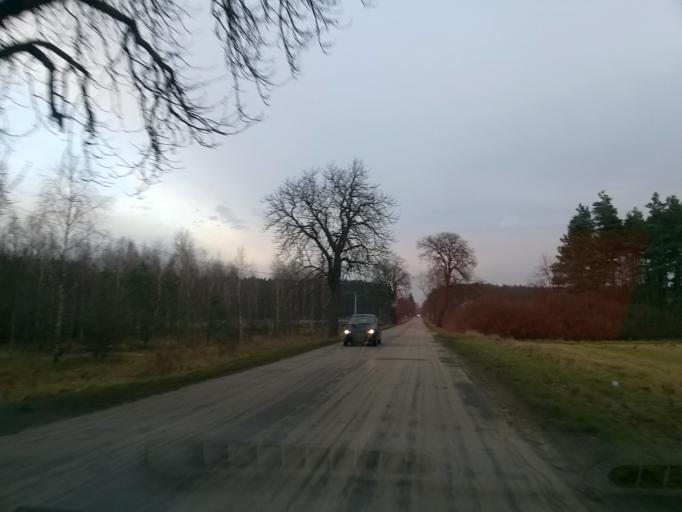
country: PL
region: Kujawsko-Pomorskie
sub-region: Powiat nakielski
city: Szubin
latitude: 53.0747
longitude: 17.7238
